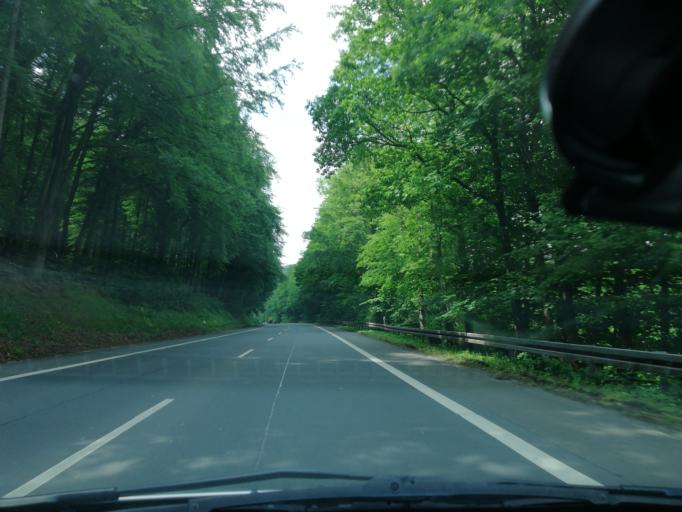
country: DE
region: North Rhine-Westphalia
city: Herdecke
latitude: 51.4179
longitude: 7.4405
